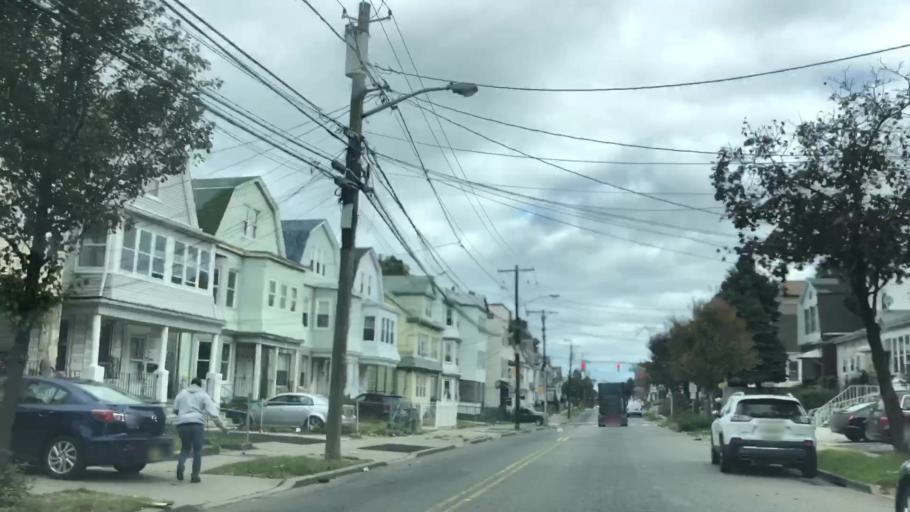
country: US
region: New Jersey
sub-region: Essex County
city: Irvington
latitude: 40.7219
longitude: -74.2246
